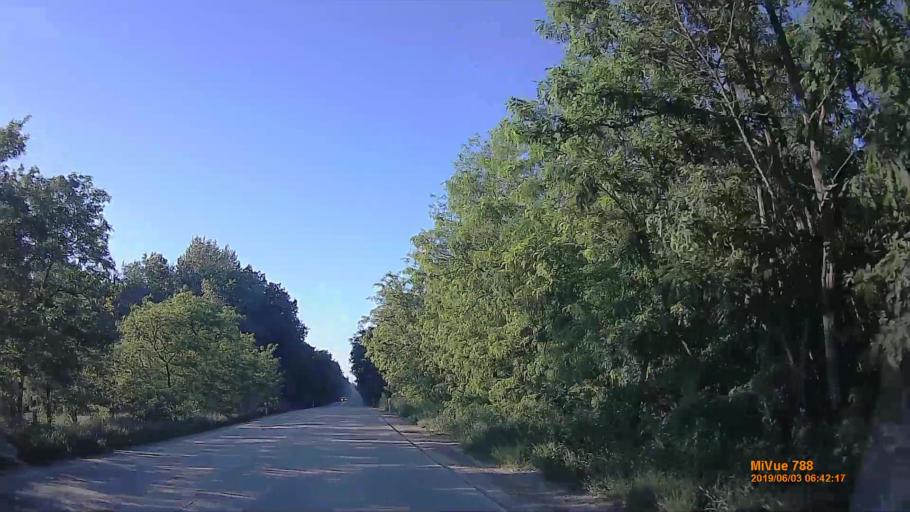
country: HU
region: Pest
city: Delegyhaza
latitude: 47.2679
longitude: 19.1134
